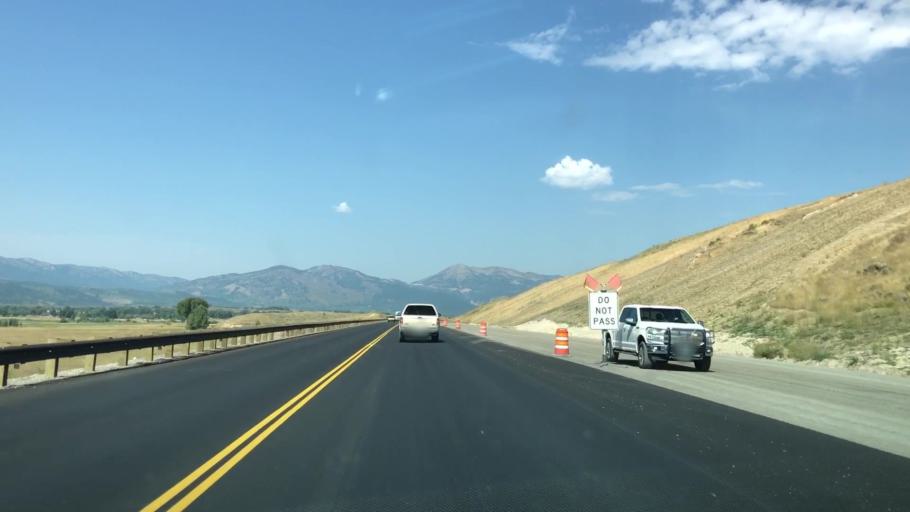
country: US
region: Wyoming
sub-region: Teton County
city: South Park
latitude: 43.4071
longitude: -110.7631
